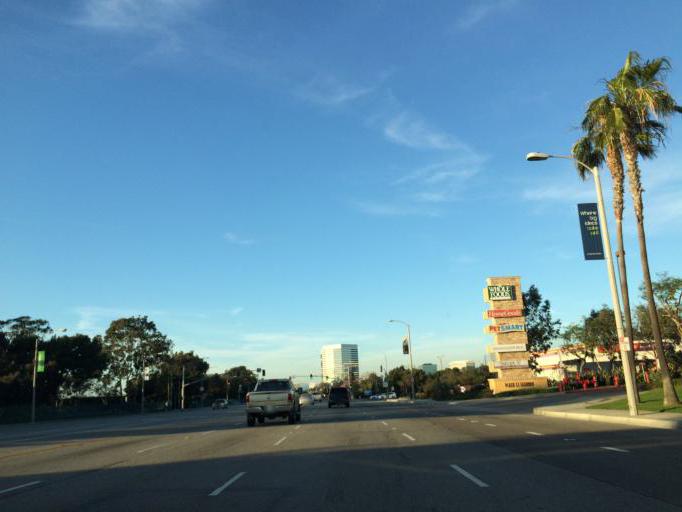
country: US
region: California
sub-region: Los Angeles County
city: El Segundo
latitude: 33.9063
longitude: -118.3959
